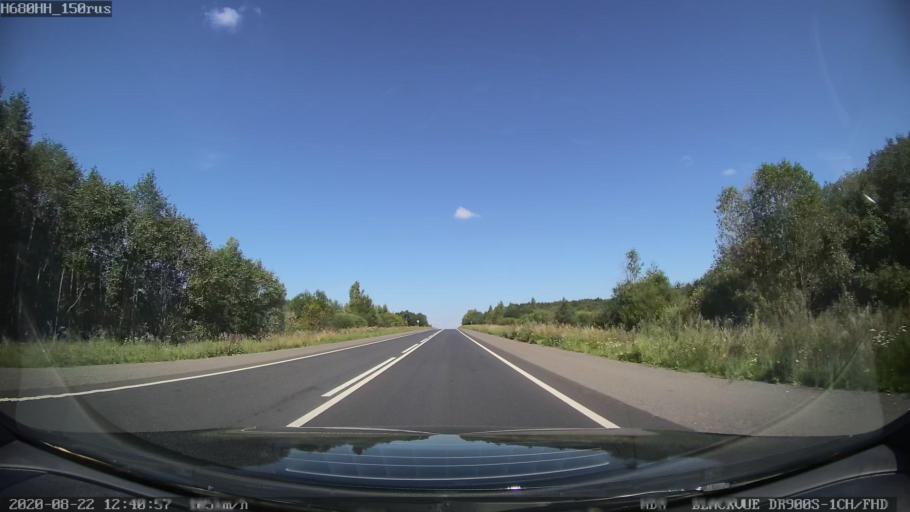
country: RU
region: Tverskaya
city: Rameshki
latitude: 57.3411
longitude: 36.0965
